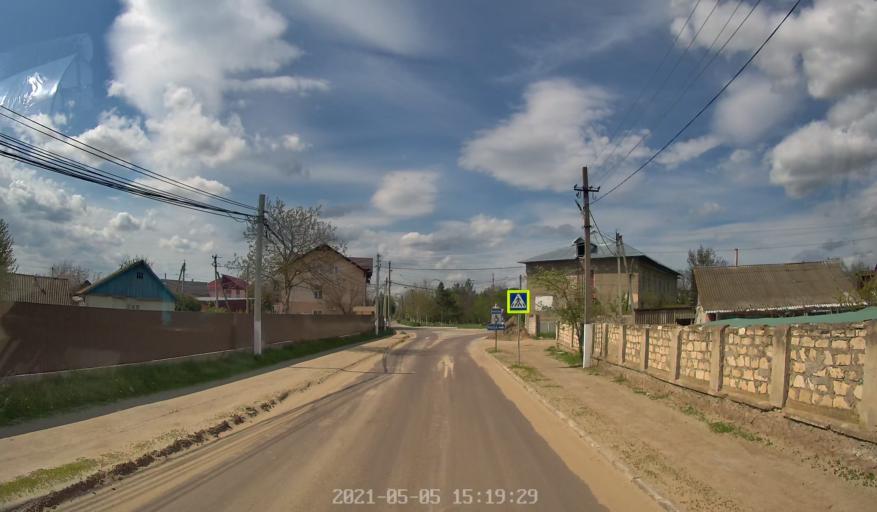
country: MD
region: Criuleni
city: Criuleni
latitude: 47.1271
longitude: 29.1939
